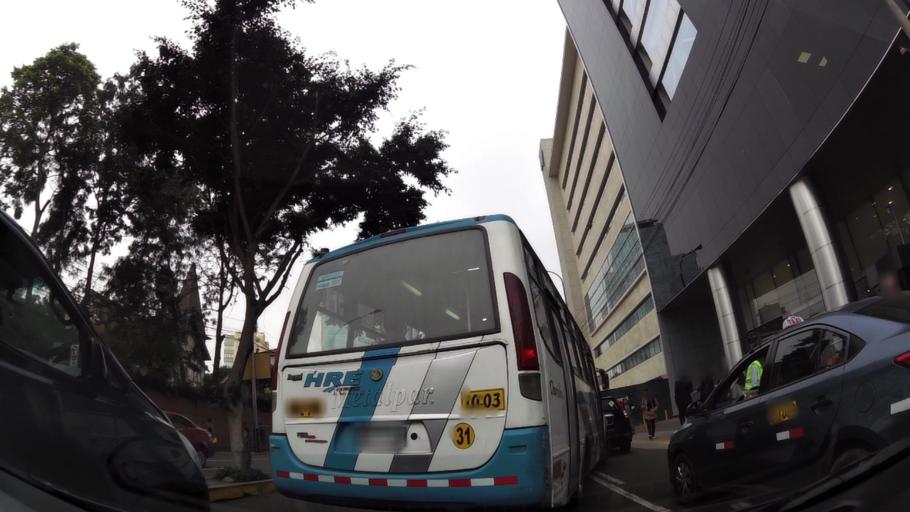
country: PE
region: Lima
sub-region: Lima
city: Surco
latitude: -12.1252
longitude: -77.0253
